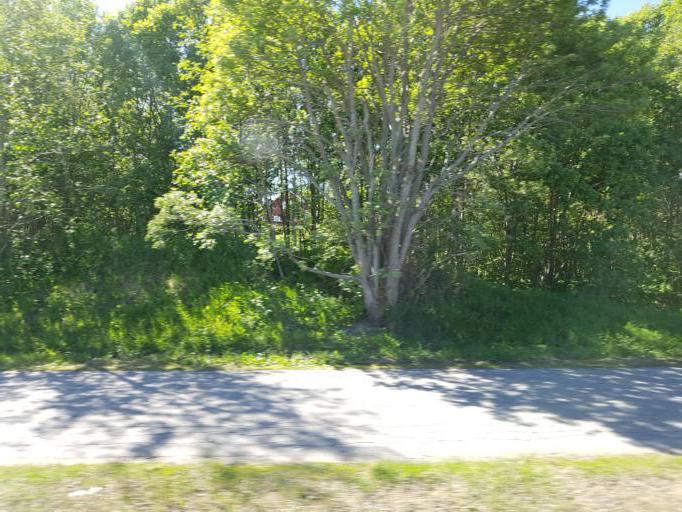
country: NO
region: Sor-Trondelag
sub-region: Trondheim
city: Trondheim
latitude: 63.4230
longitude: 10.5223
